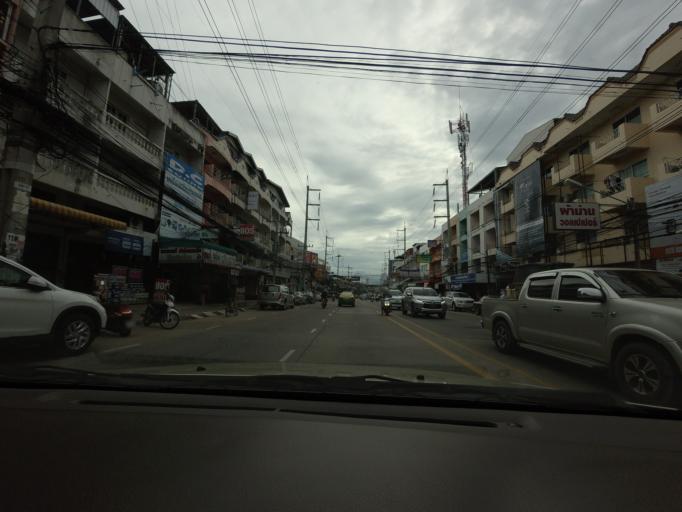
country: TH
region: Chon Buri
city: Phatthaya
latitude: 12.9083
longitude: 100.8861
